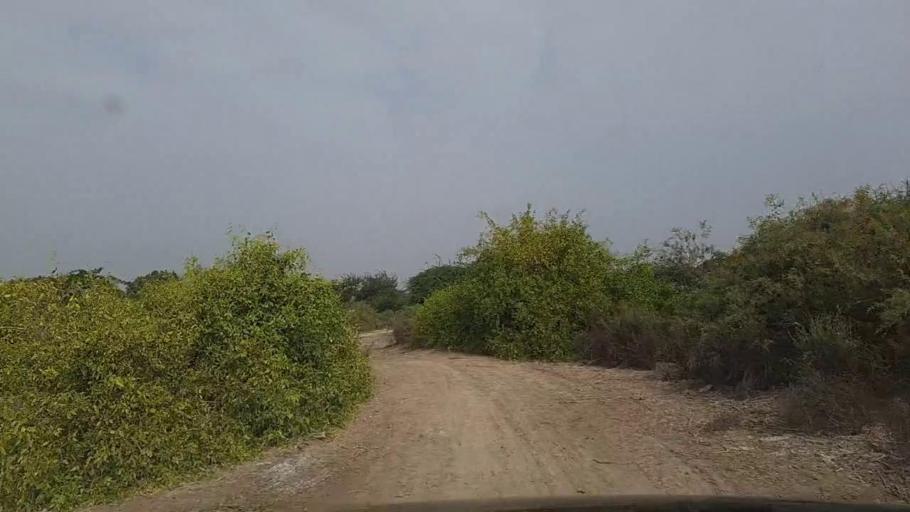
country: PK
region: Sindh
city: Thatta
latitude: 24.7542
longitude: 67.8276
